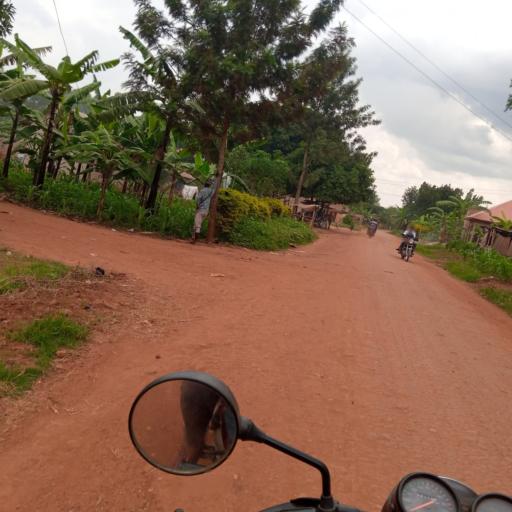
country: UG
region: Eastern Region
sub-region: Mbale District
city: Mbale
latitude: 1.1083
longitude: 34.1803
